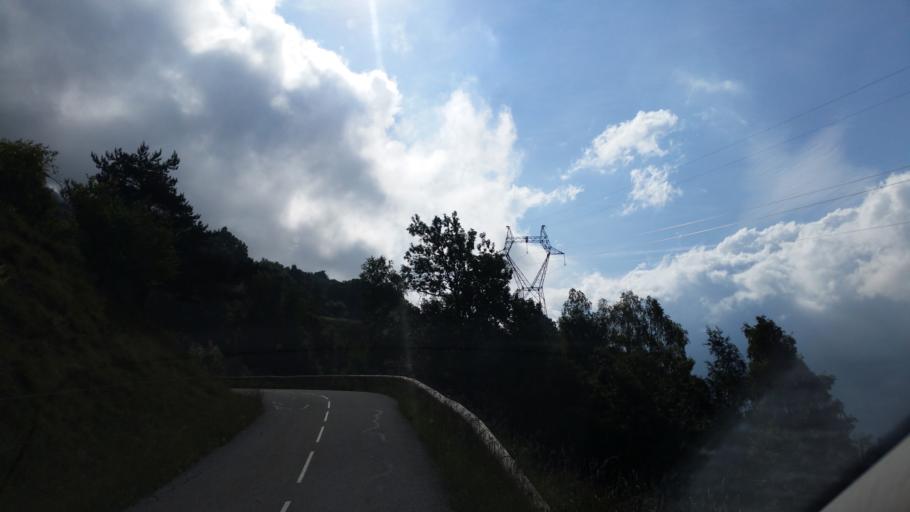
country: FR
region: Rhone-Alpes
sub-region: Departement de la Savoie
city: Modane
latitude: 45.2105
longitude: 6.6023
